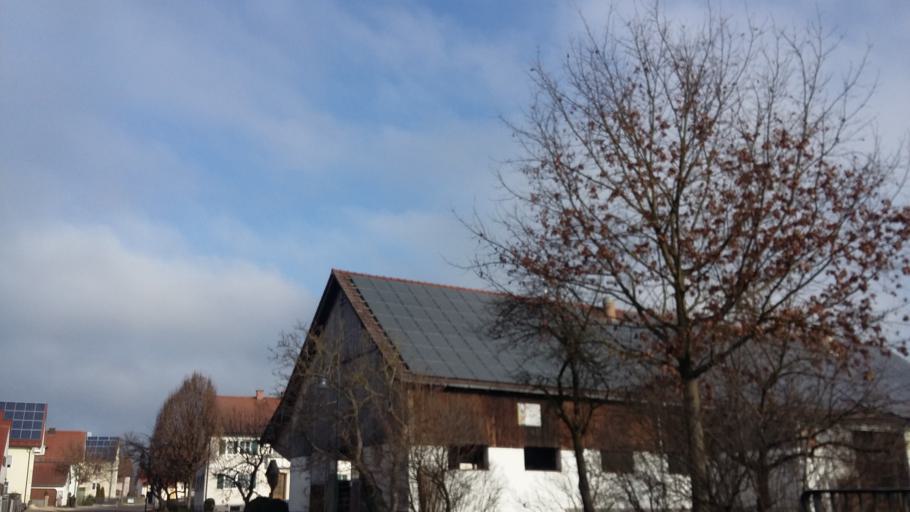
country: DE
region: Bavaria
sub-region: Swabia
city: Sielenbach
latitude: 48.3960
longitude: 11.1643
